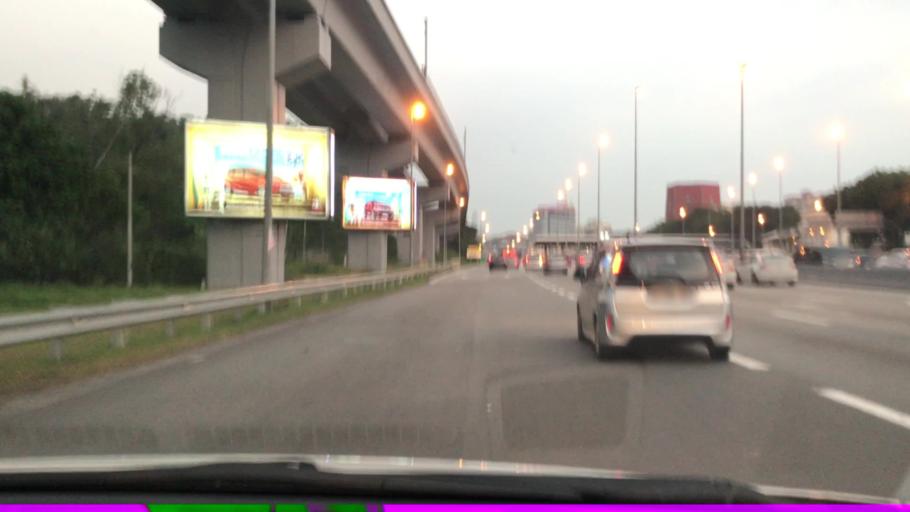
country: MY
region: Selangor
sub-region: Petaling
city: Petaling Jaya
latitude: 3.1321
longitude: 101.6369
